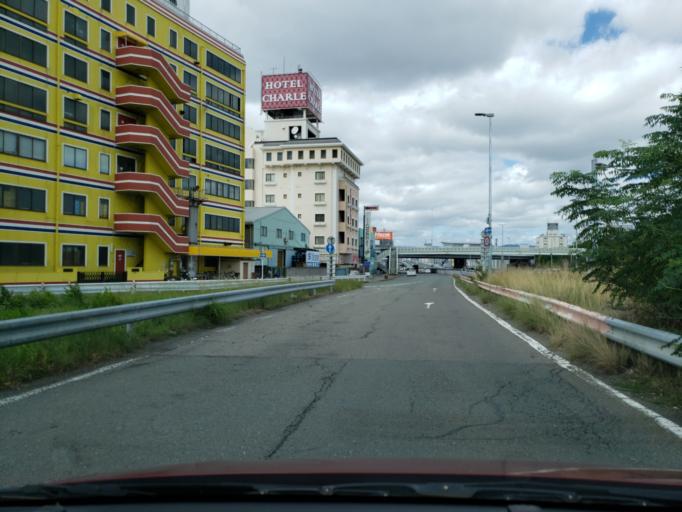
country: JP
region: Osaka
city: Toyonaka
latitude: 34.7509
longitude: 135.4630
